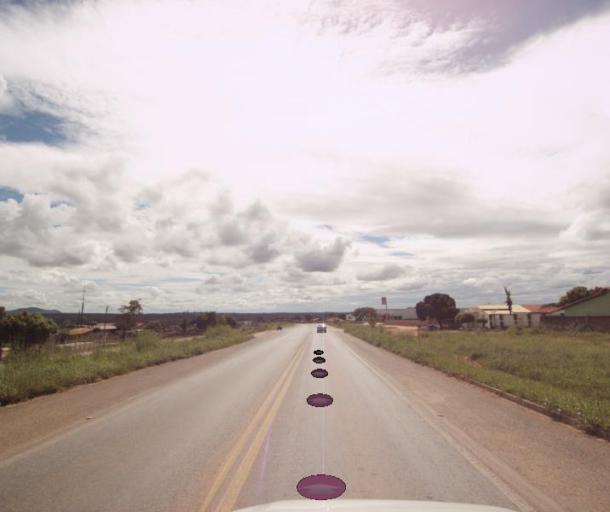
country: BR
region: Goias
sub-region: Uruacu
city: Uruacu
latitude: -14.5158
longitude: -49.1515
